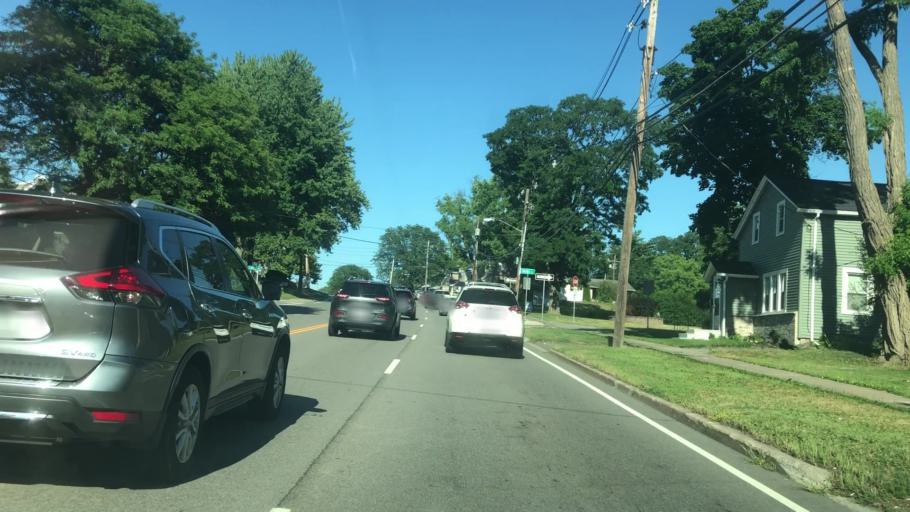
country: US
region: New York
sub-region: Monroe County
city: East Rochester
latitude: 43.1289
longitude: -77.4806
